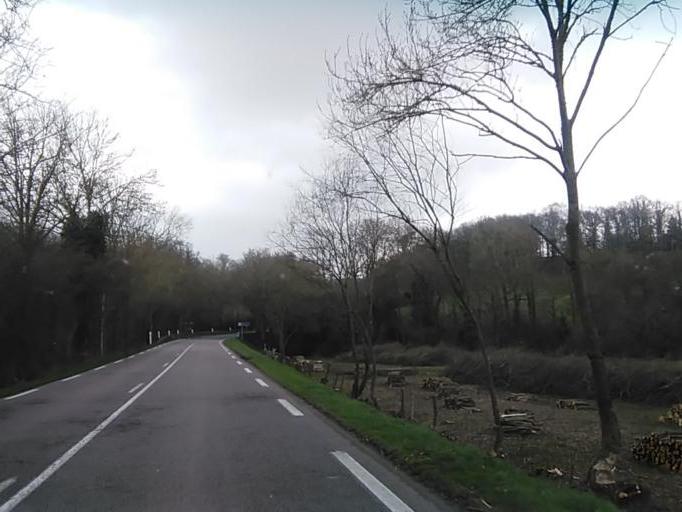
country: FR
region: Lower Normandy
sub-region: Departement du Calvados
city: Falaise
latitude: 48.8455
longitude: -0.2322
